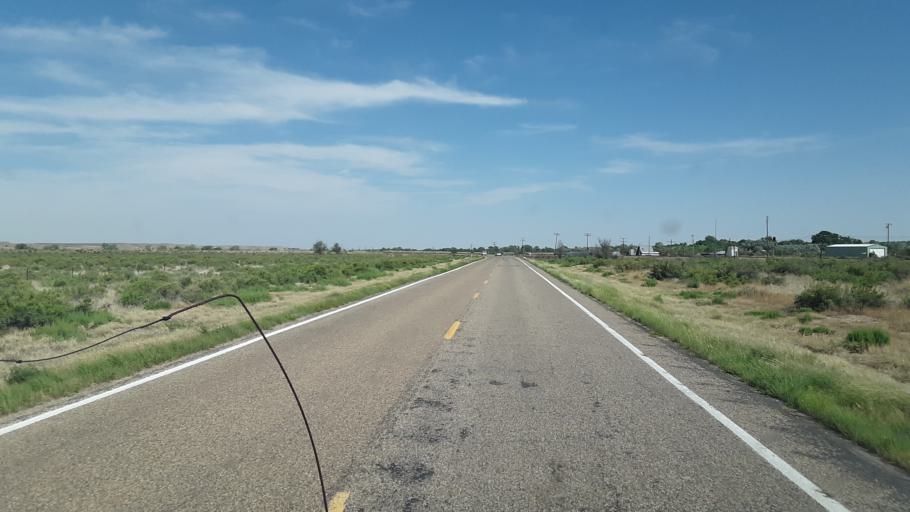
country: US
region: Colorado
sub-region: Otero County
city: Fowler
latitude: 38.1952
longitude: -104.1575
